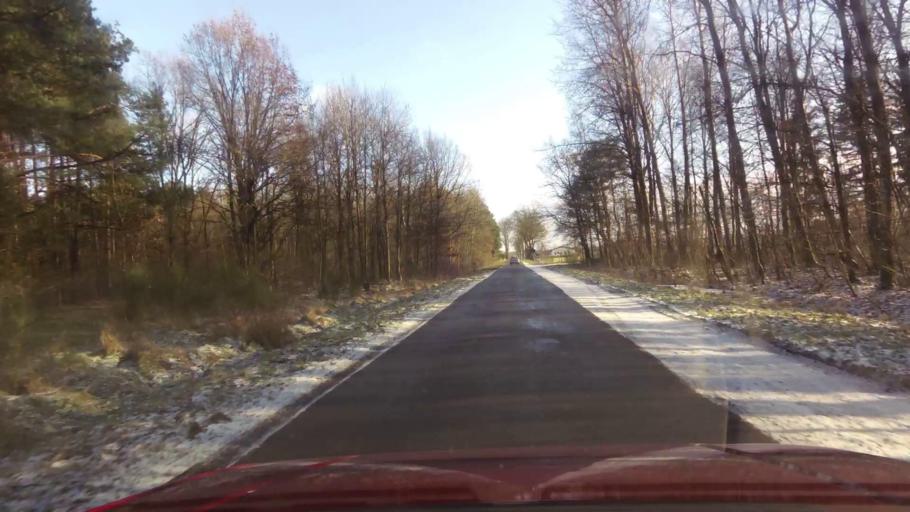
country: PL
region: West Pomeranian Voivodeship
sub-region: Powiat bialogardzki
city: Bialogard
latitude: 54.0848
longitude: 16.0807
